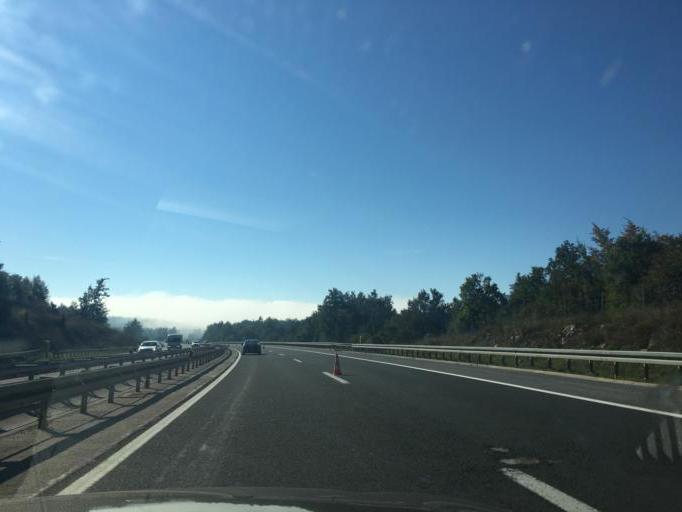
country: HR
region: Licko-Senjska
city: Gospic
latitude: 44.6440
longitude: 15.4349
